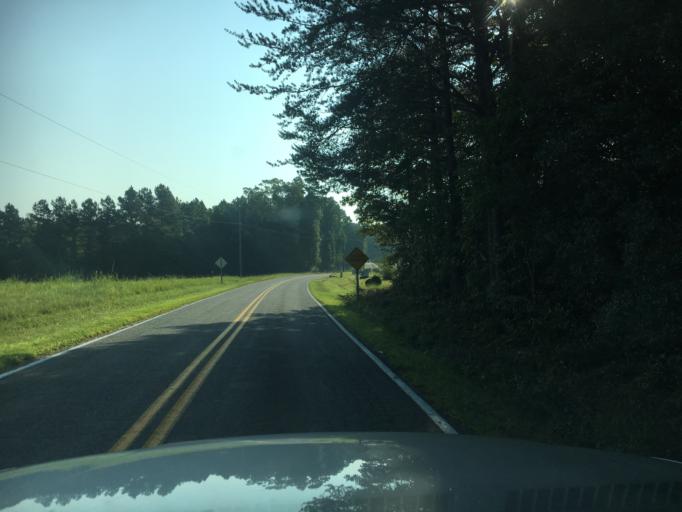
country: US
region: North Carolina
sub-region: Rutherford County
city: Rutherfordton
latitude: 35.2504
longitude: -82.0473
